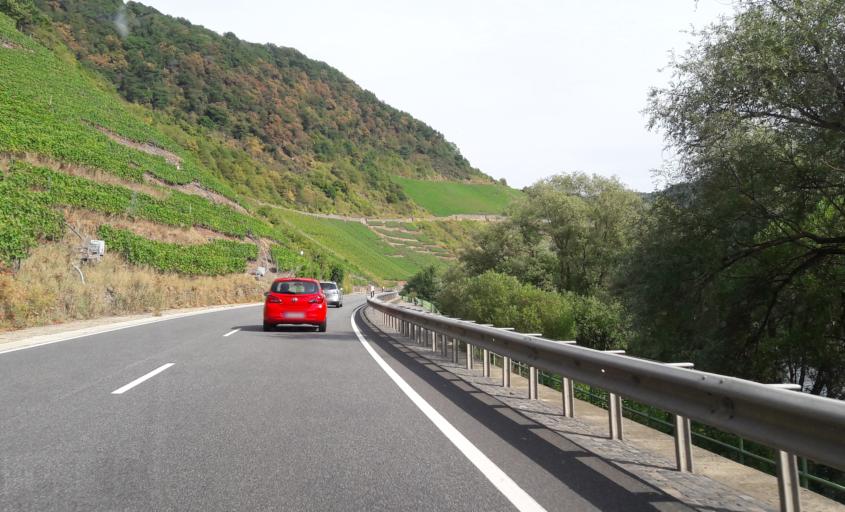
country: DE
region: Rheinland-Pfalz
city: Bruttig-Fankel
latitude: 50.1281
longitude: 7.2246
